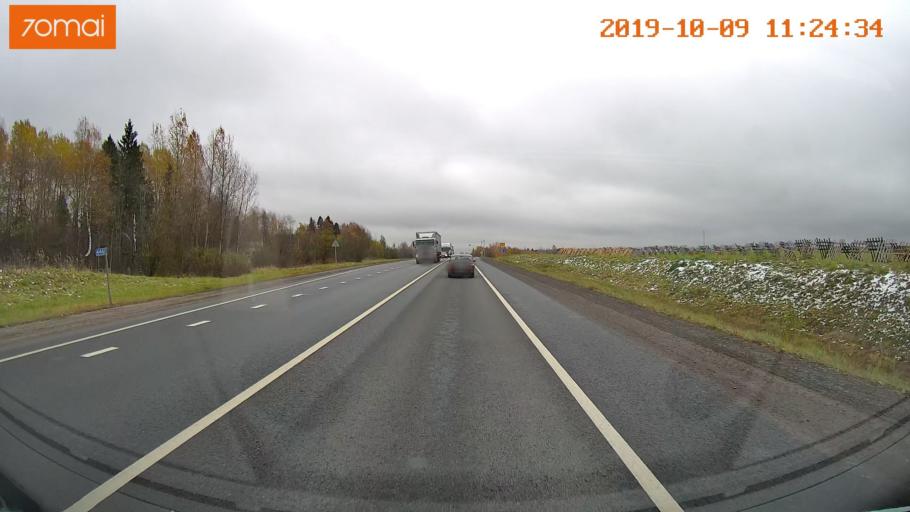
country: RU
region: Vologda
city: Vologda
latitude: 59.1103
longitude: 39.9813
